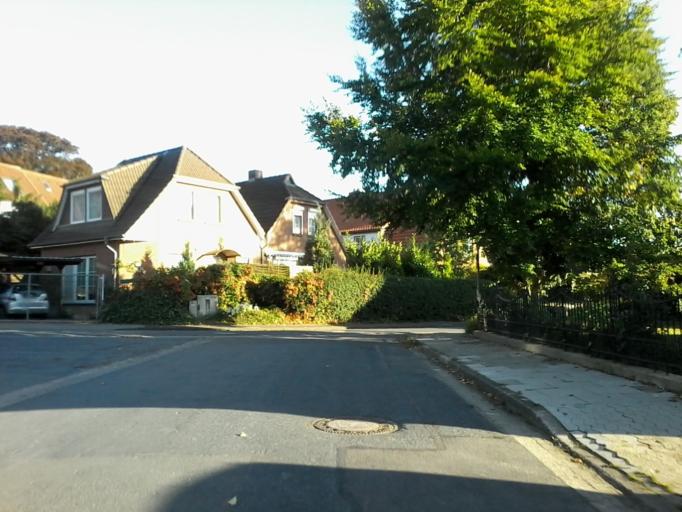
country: DE
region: Lower Saxony
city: Achim
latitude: 53.0091
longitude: 9.0324
